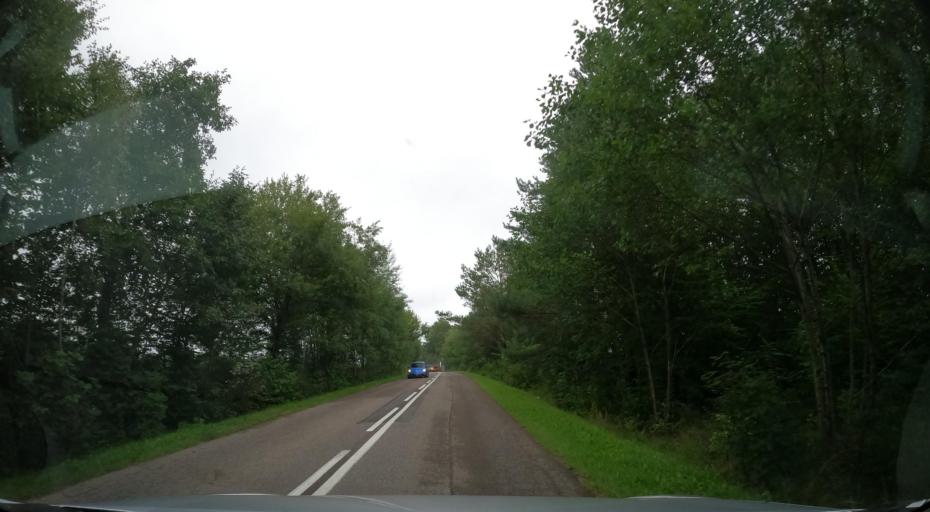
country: PL
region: Pomeranian Voivodeship
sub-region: Powiat wejherowski
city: Luzino
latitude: 54.4853
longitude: 18.1113
